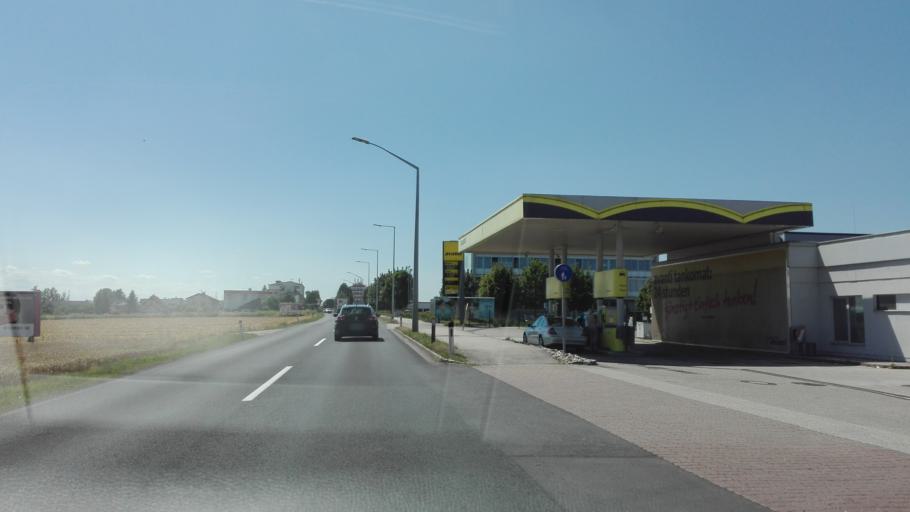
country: AT
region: Upper Austria
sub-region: Politischer Bezirk Linz-Land
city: Leonding
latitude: 48.2735
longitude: 14.2529
